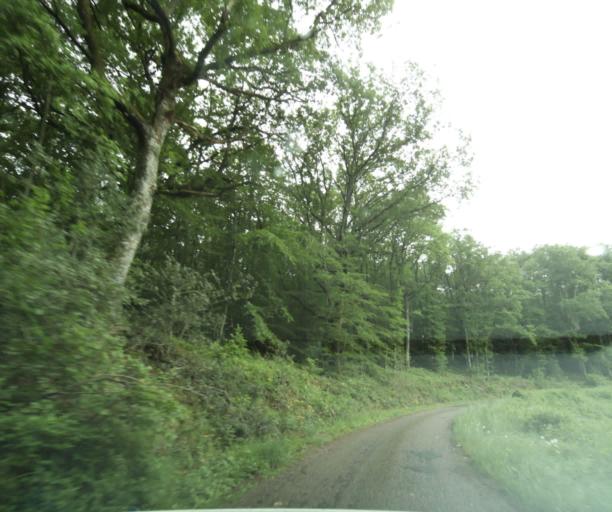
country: FR
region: Bourgogne
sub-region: Departement de Saone-et-Loire
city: Matour
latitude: 46.4444
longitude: 4.4685
